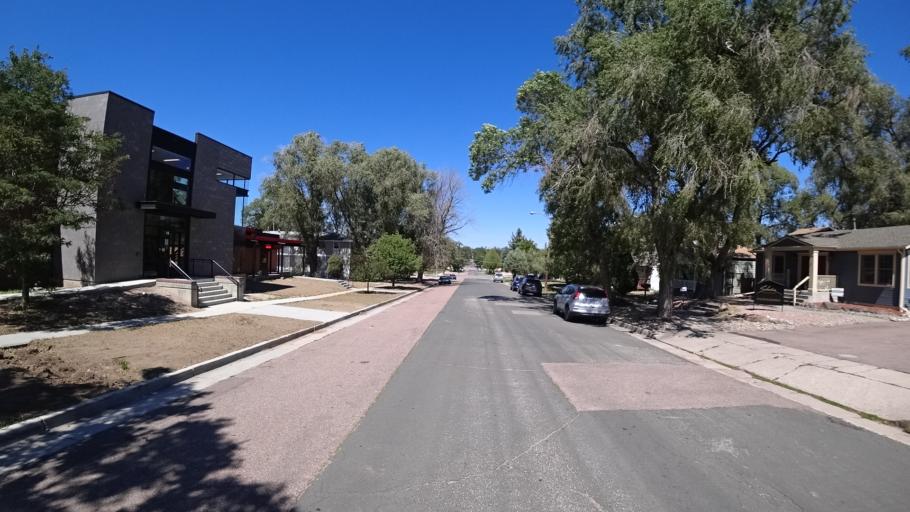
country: US
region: Colorado
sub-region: El Paso County
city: Colorado Springs
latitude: 38.8335
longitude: -104.7962
